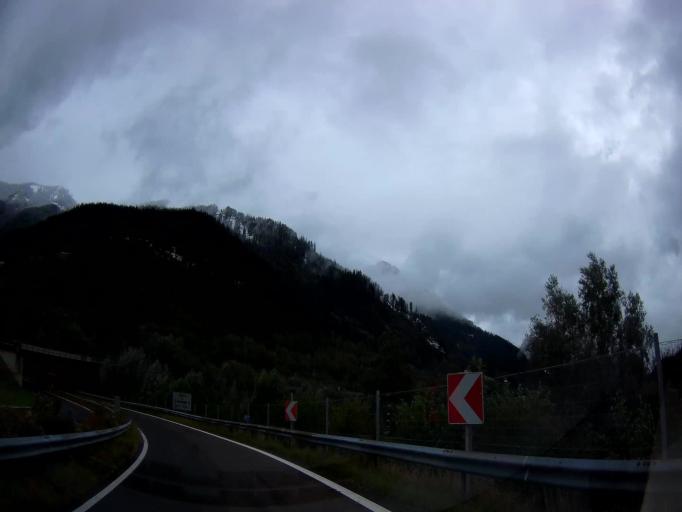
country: AT
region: Styria
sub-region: Politischer Bezirk Liezen
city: Treglwang
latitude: 47.4731
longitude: 14.5988
